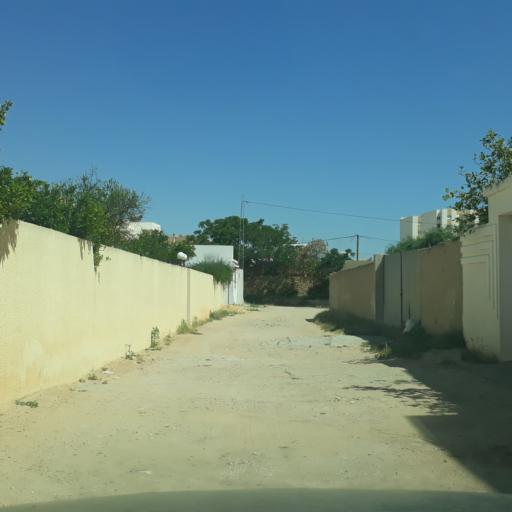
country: TN
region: Safaqis
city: Al Qarmadah
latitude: 34.7980
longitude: 10.7601
